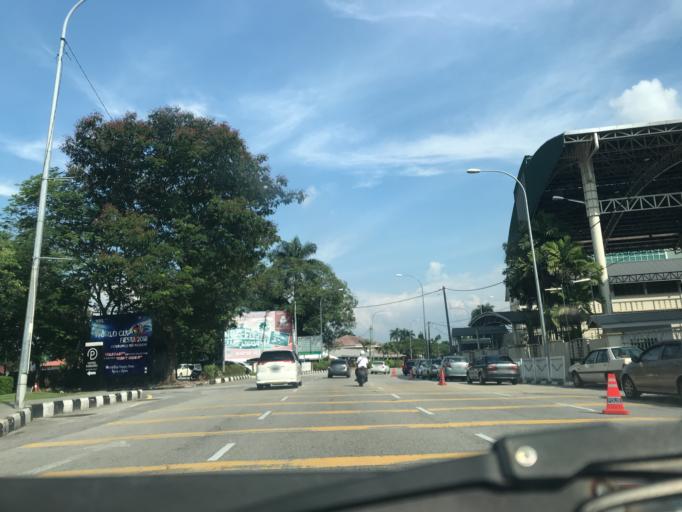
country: MY
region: Perak
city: Ipoh
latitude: 4.5947
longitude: 101.0898
